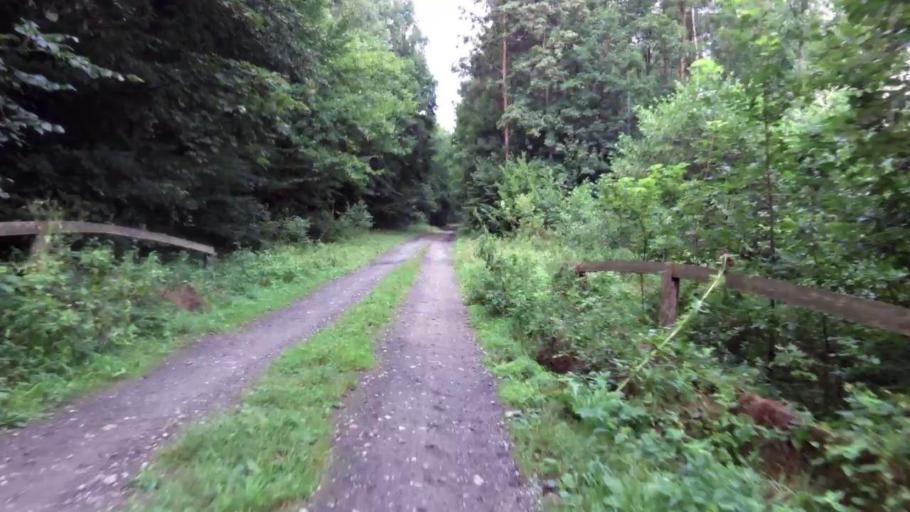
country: PL
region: West Pomeranian Voivodeship
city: Trzcinsko Zdroj
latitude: 52.8732
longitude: 14.6878
